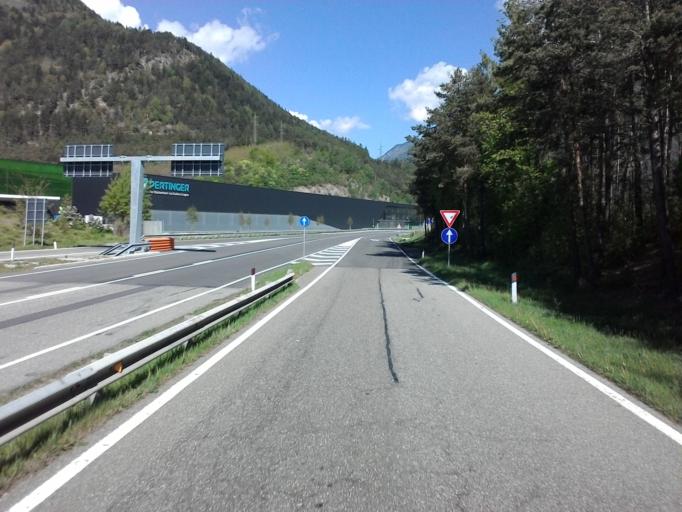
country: IT
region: Trentino-Alto Adige
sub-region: Bolzano
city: Naz-Sciaves - Natz-Schabs
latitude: 46.7669
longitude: 11.6413
